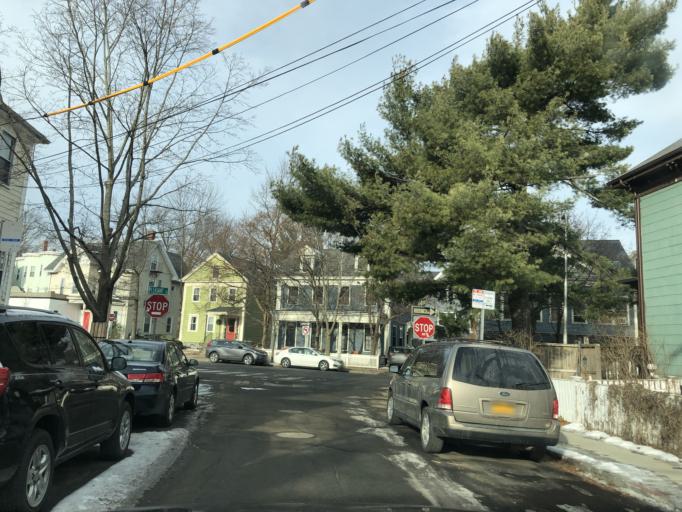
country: US
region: Massachusetts
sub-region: Middlesex County
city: Cambridge
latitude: 42.3638
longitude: -71.1080
